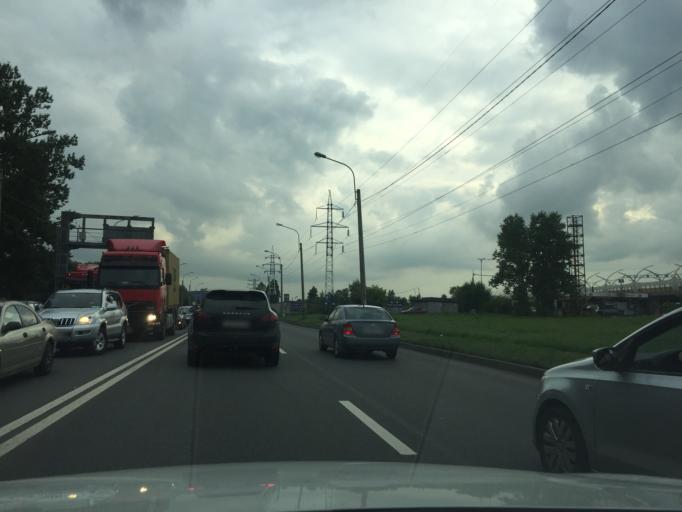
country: RU
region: St.-Petersburg
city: Avtovo
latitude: 59.8509
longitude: 30.2923
